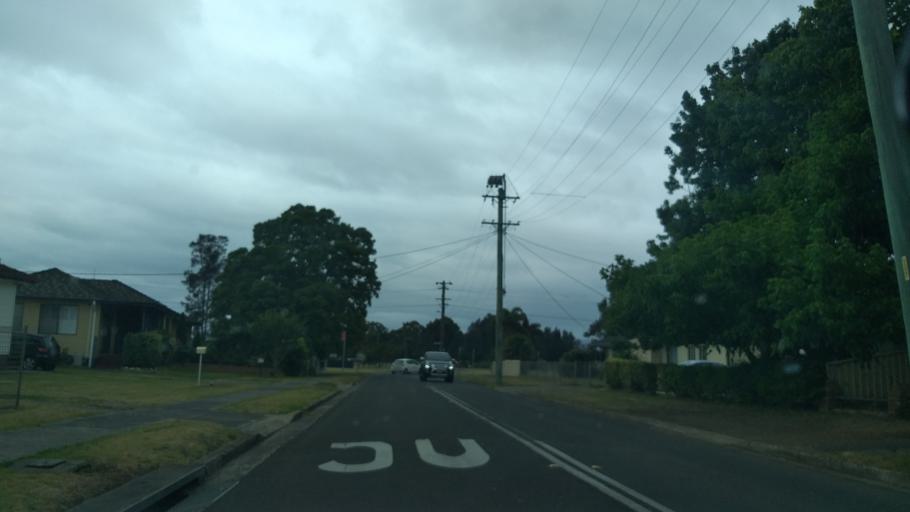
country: AU
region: New South Wales
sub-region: Wollongong
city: Berkeley
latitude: -34.4771
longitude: 150.8388
